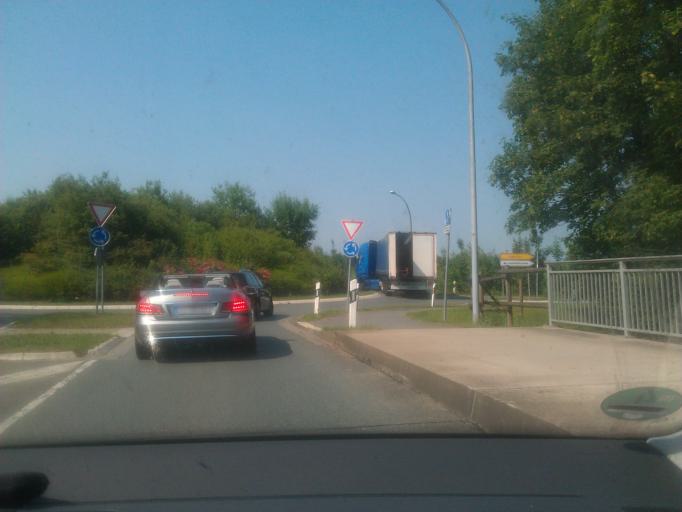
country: DE
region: North Rhine-Westphalia
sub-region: Regierungsbezirk Detmold
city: Leopoldshohe
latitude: 52.0011
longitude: 8.6964
